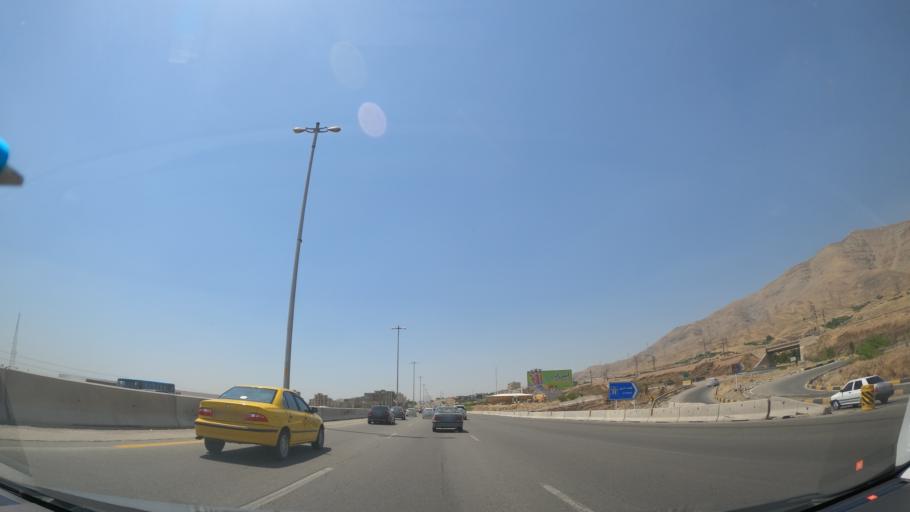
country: IR
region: Tehran
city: Shahr-e Qods
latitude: 35.7522
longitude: 51.0779
